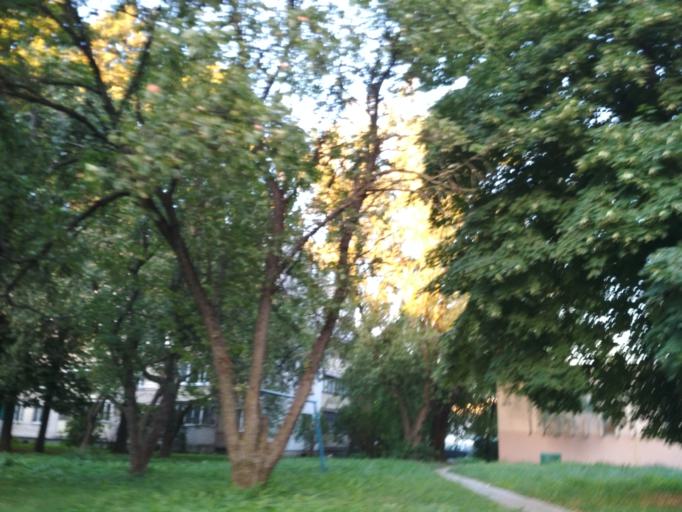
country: BY
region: Minsk
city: Minsk
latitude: 53.8792
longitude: 27.5379
